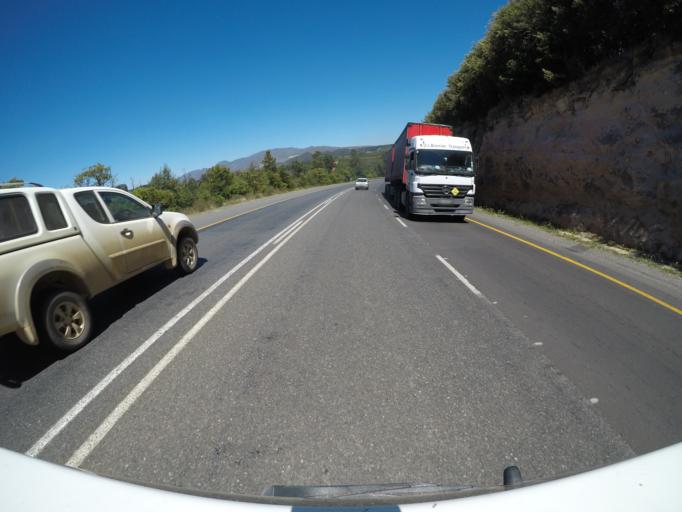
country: ZA
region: Western Cape
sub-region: Overberg District Municipality
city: Grabouw
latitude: -34.1648
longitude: 19.0252
